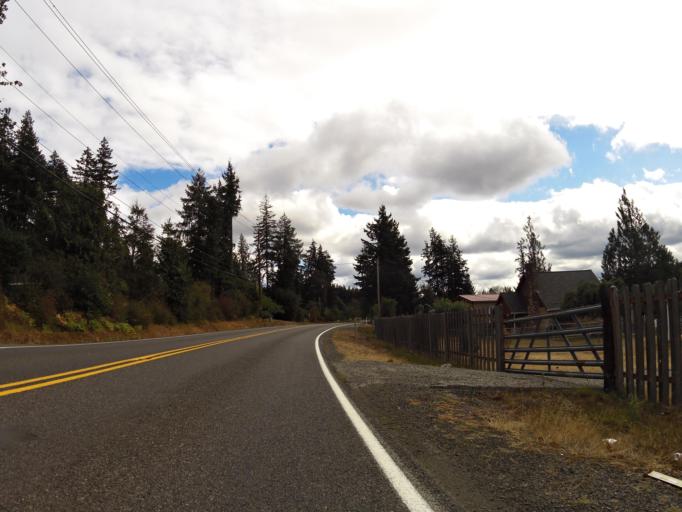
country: US
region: Washington
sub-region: Mason County
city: Shelton
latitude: 47.1806
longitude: -123.0915
